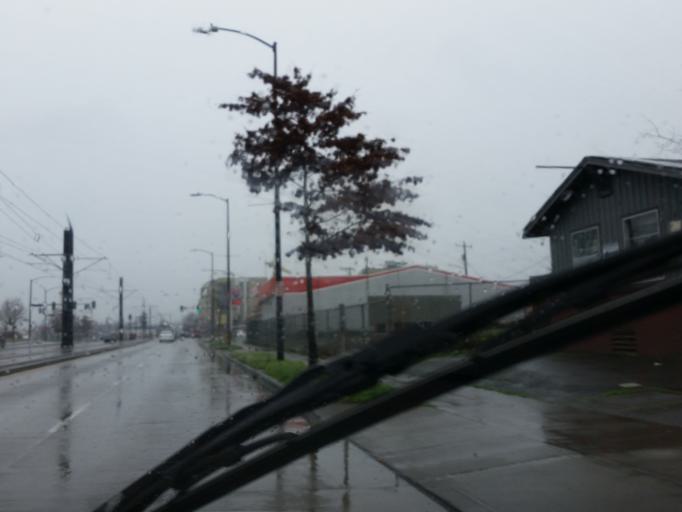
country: US
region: Washington
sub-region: King County
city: Riverton
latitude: 47.5341
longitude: -122.2806
